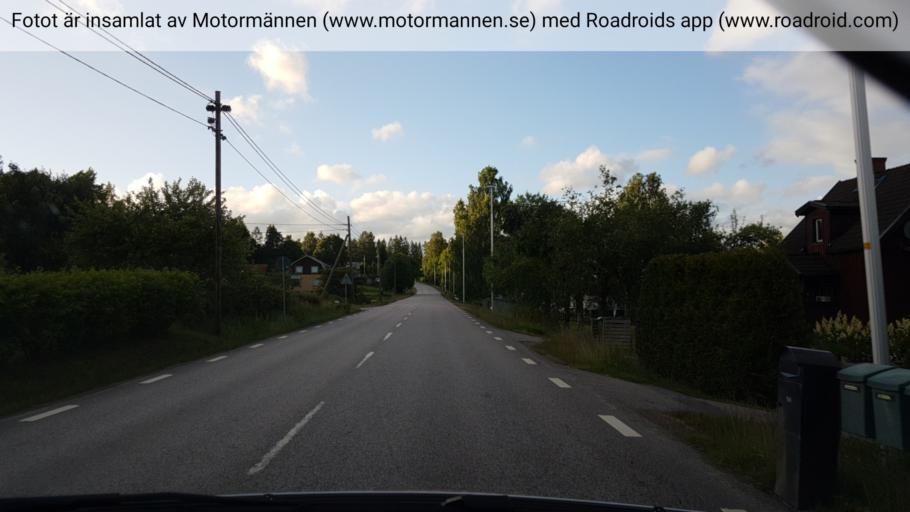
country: SE
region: OErebro
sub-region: Karlskoga Kommun
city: Karlskoga
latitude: 59.3553
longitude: 14.5721
